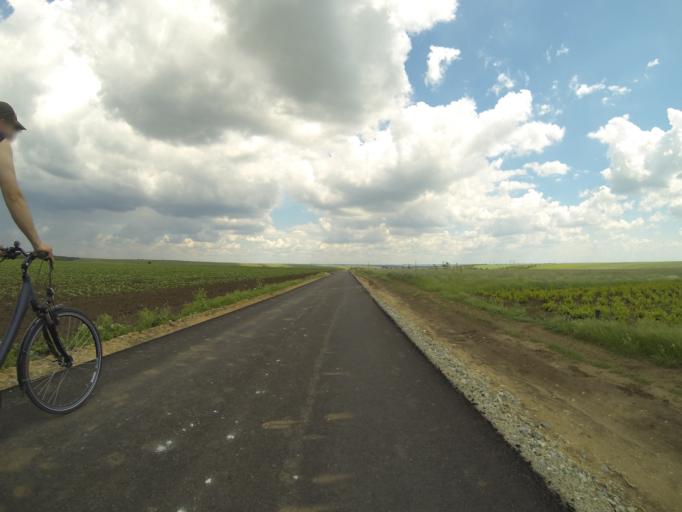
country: RO
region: Dolj
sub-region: Comuna Dranicu
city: Padea
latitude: 44.0254
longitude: 23.8469
